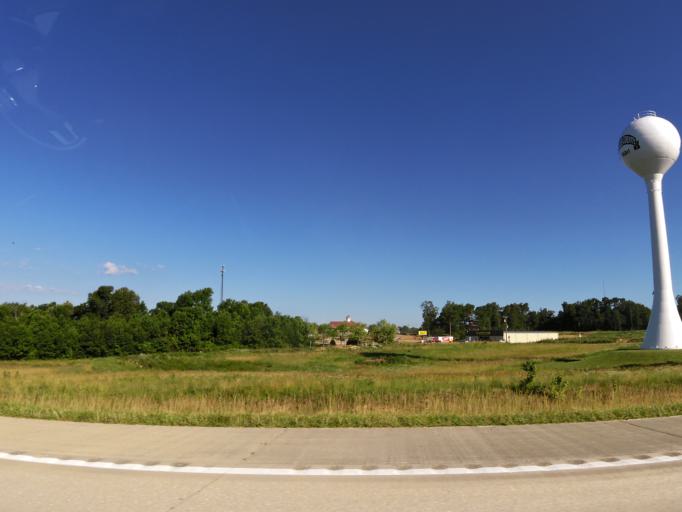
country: US
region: Missouri
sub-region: Butler County
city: Poplar Bluff
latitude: 36.6628
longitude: -90.5164
